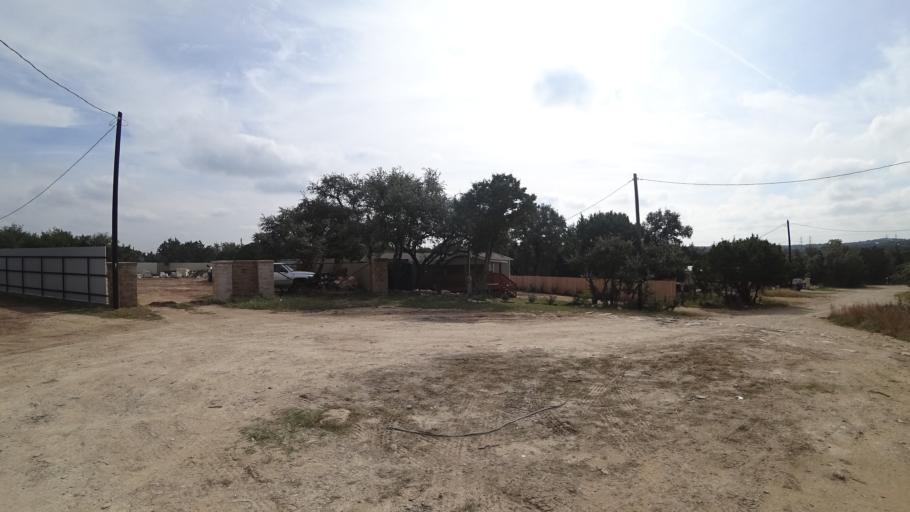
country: US
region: Texas
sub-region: Travis County
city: Hudson Bend
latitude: 30.3863
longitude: -97.9333
